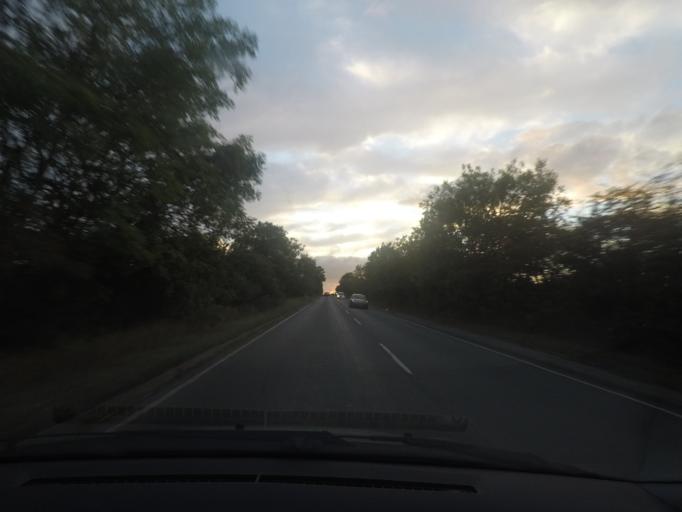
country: GB
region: England
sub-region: North Lincolnshire
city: Barnetby le Wold
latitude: 53.5824
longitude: -0.3988
